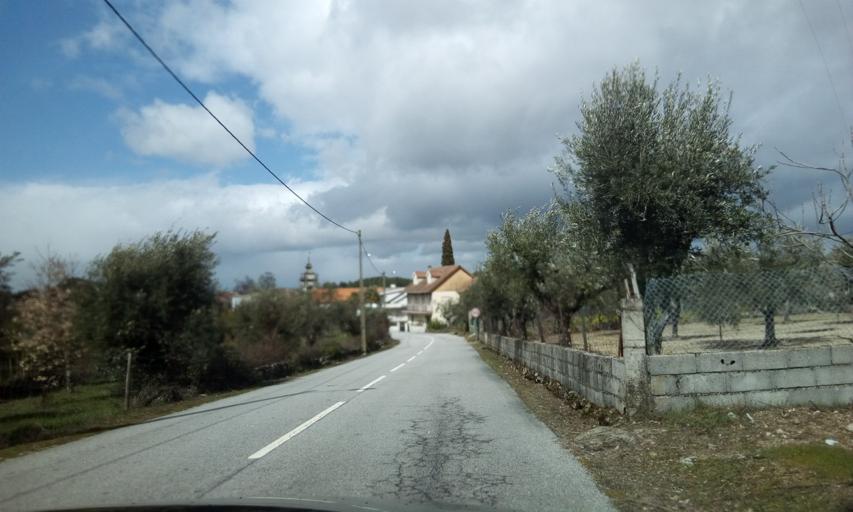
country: PT
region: Guarda
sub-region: Fornos de Algodres
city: Fornos de Algodres
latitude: 40.6449
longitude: -7.5478
